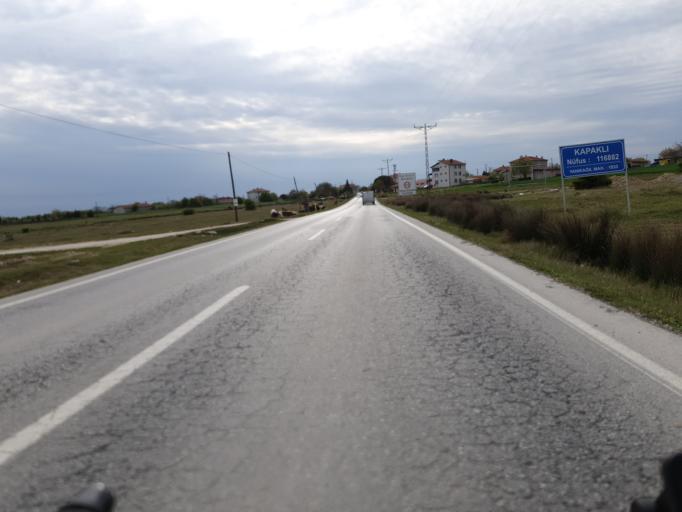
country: TR
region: Tekirdag
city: Velimese
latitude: 41.2903
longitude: 27.9128
